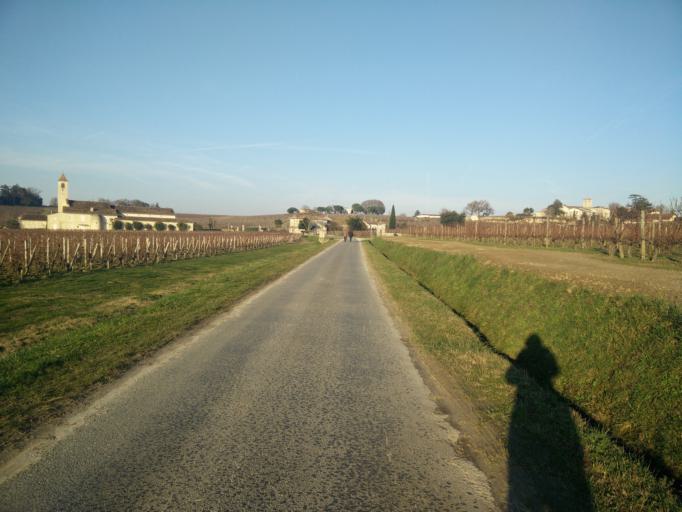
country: FR
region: Aquitaine
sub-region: Departement de la Gironde
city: Saint-Emilion
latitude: 44.8892
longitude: -0.1695
